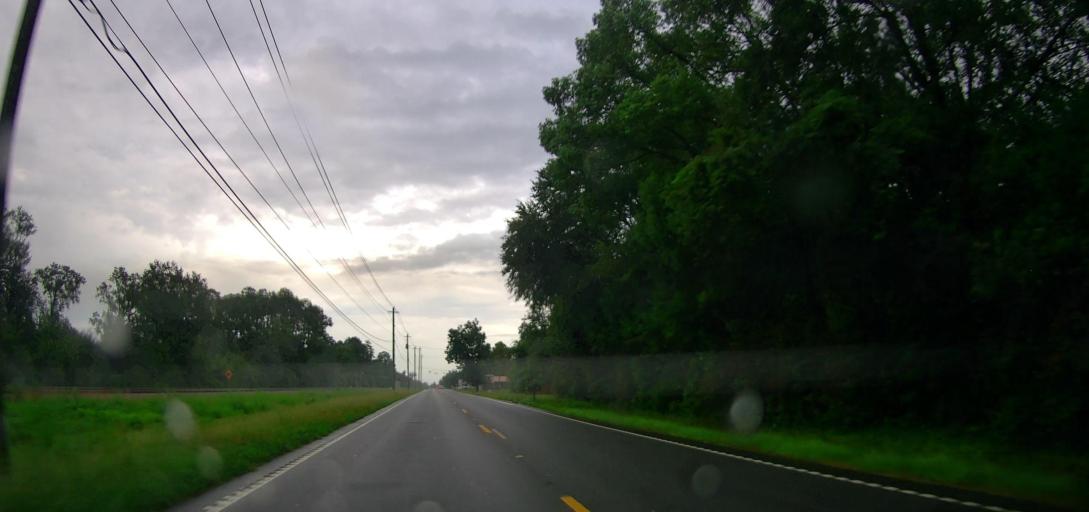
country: US
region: Georgia
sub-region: Ware County
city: Deenwood
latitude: 31.2429
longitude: -82.3728
